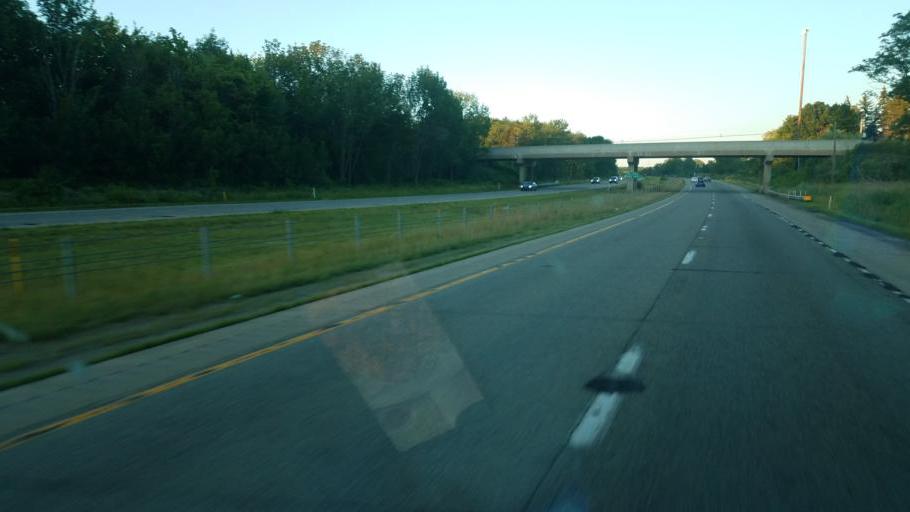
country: US
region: Pennsylvania
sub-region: Erie County
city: Fairview
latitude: 42.0237
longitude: -80.1436
